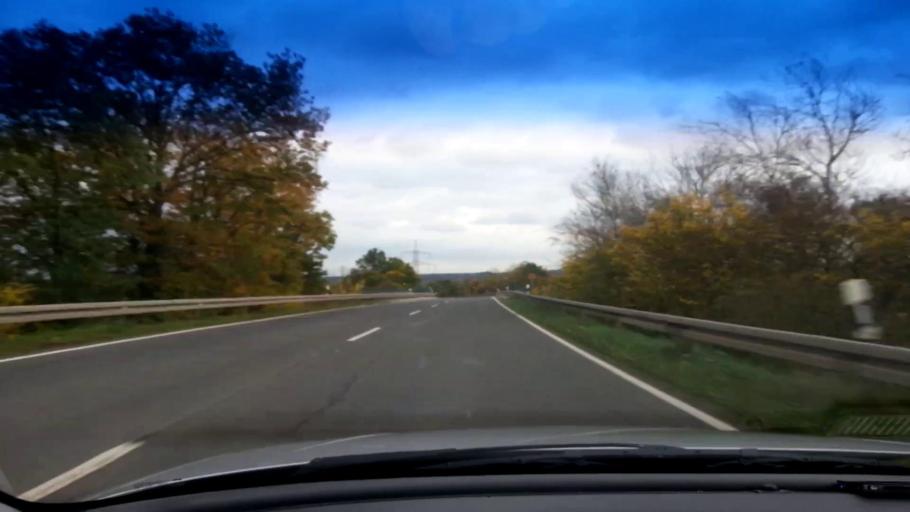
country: DE
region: Bavaria
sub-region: Upper Franconia
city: Viereth-Trunstadt
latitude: 49.9419
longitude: 10.7606
